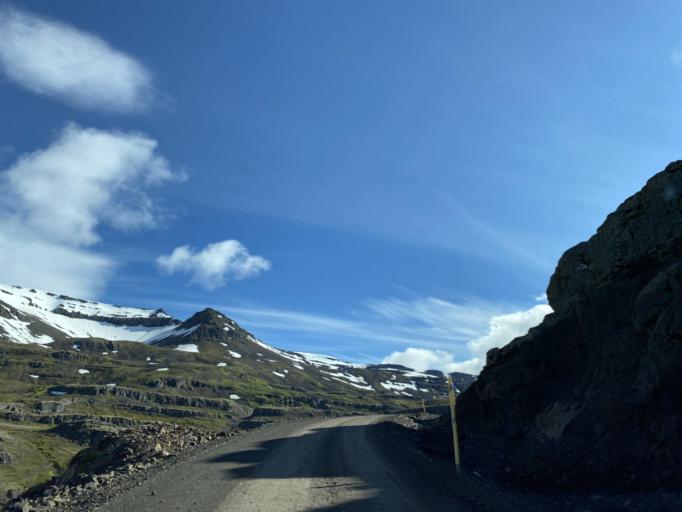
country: IS
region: East
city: Eskifjoerdur
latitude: 65.1788
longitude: -14.0966
